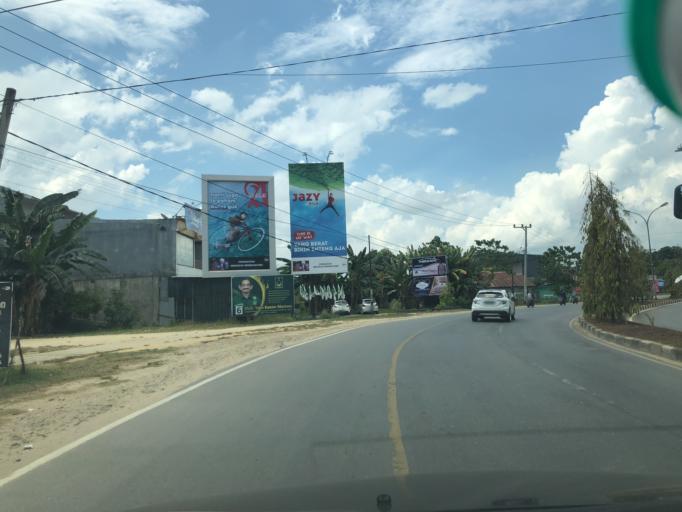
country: ID
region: Sulawesi Tenggara
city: Kendari
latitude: -3.9885
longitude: 122.5186
